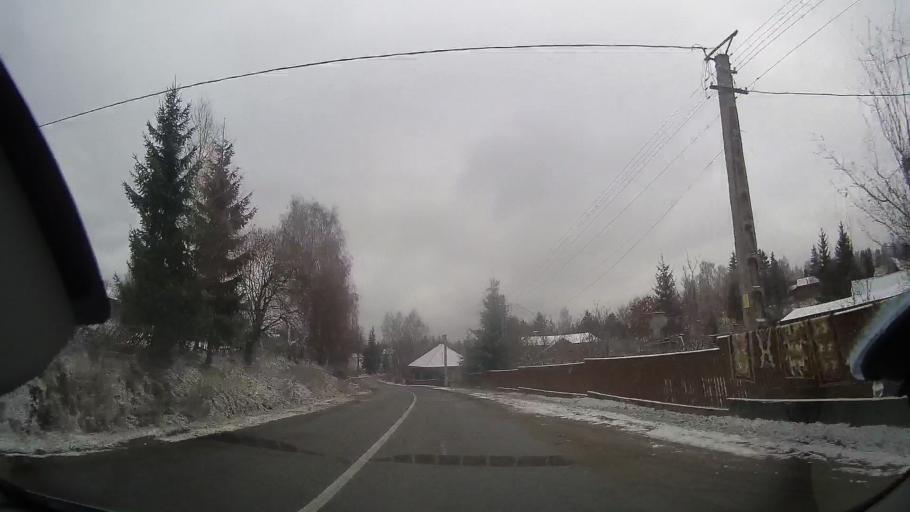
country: RO
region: Cluj
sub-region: Comuna Calatele
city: Calatele
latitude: 46.7113
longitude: 23.0413
